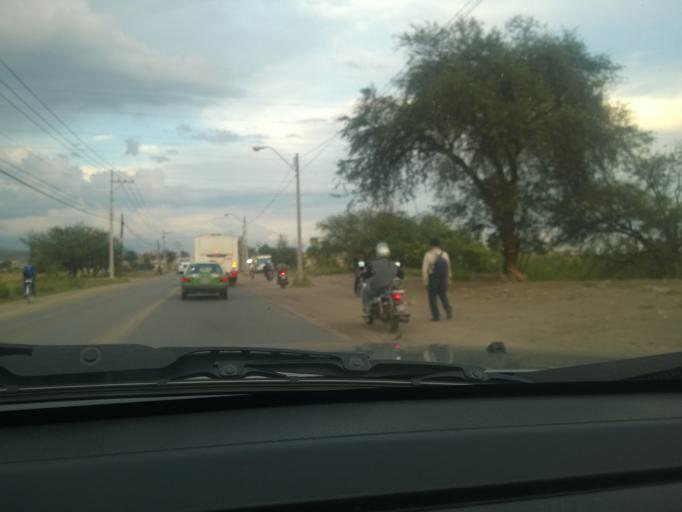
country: MX
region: Guanajuato
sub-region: Leon
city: Fraccionamiento Paraiso Real
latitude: 21.1102
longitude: -101.5995
